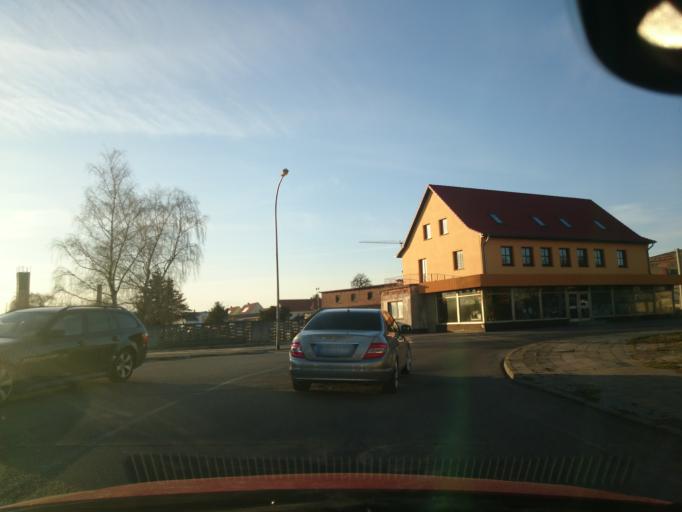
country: DE
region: Mecklenburg-Vorpommern
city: Barth
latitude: 54.3636
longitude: 12.7255
